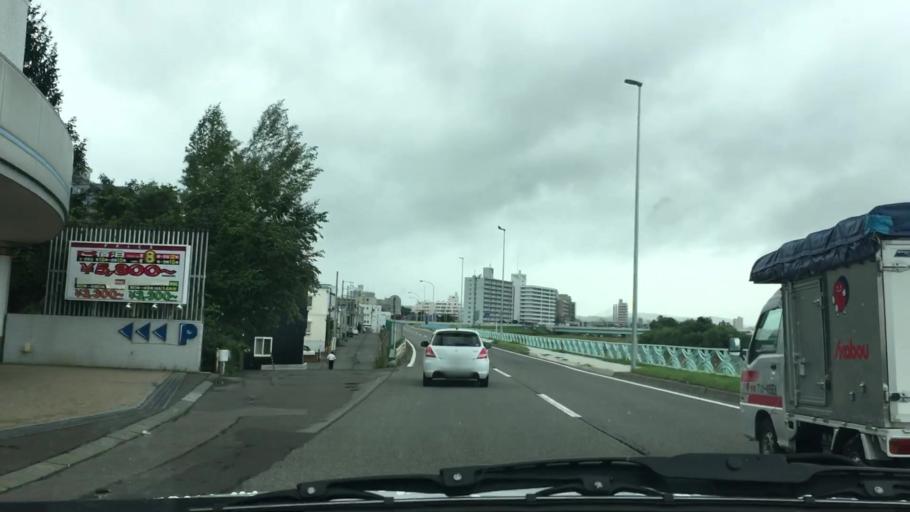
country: JP
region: Hokkaido
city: Sapporo
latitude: 43.0343
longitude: 141.3570
